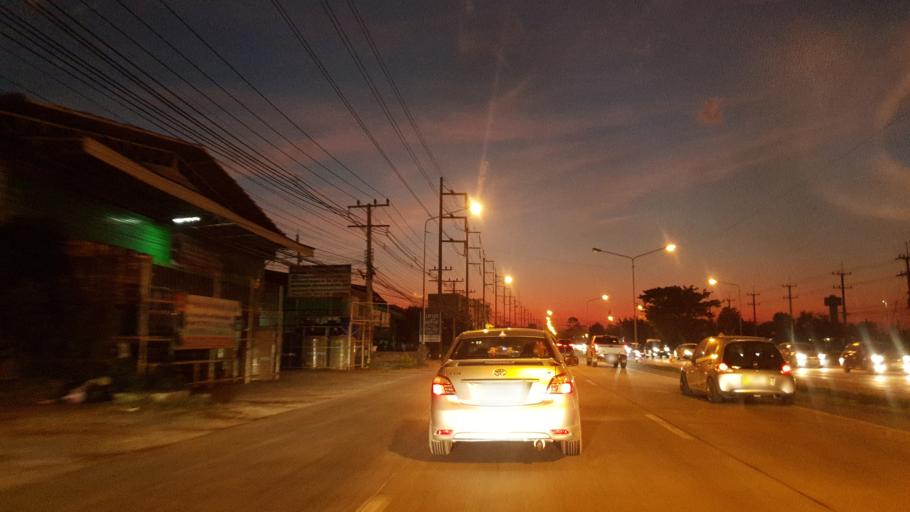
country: TH
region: Phitsanulok
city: Wang Thong
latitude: 16.8209
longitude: 100.3473
